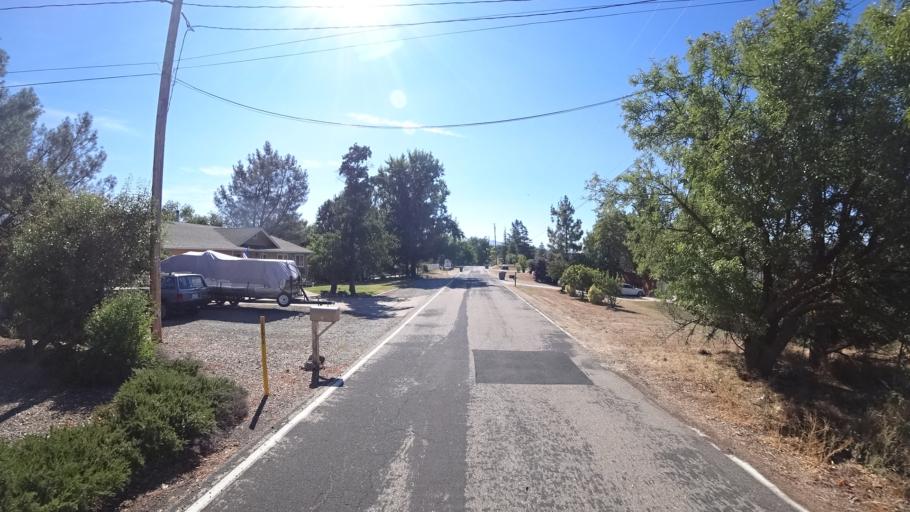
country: US
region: California
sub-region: Calaveras County
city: Valley Springs
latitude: 38.1663
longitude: -120.8531
